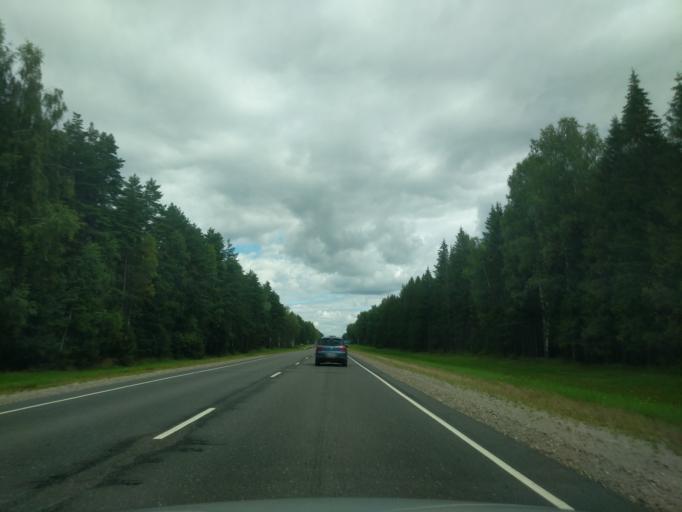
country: RU
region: Jaroslavl
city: Nekrasovskoye
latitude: 57.6019
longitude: 40.3192
